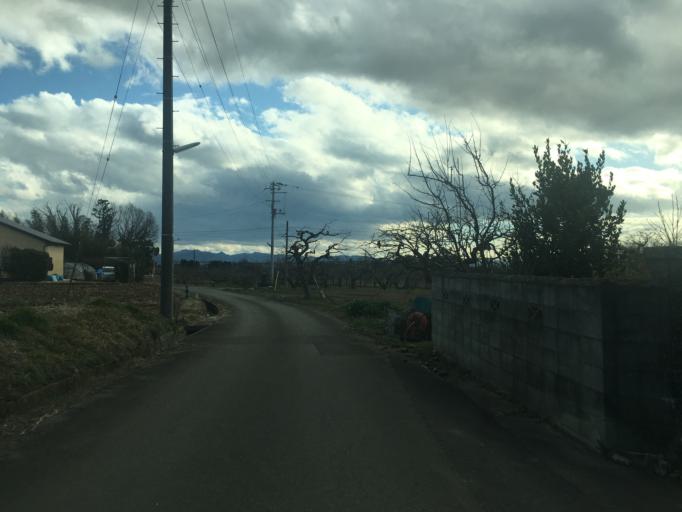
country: JP
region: Fukushima
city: Yanagawamachi-saiwaicho
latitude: 37.8847
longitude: 140.5800
